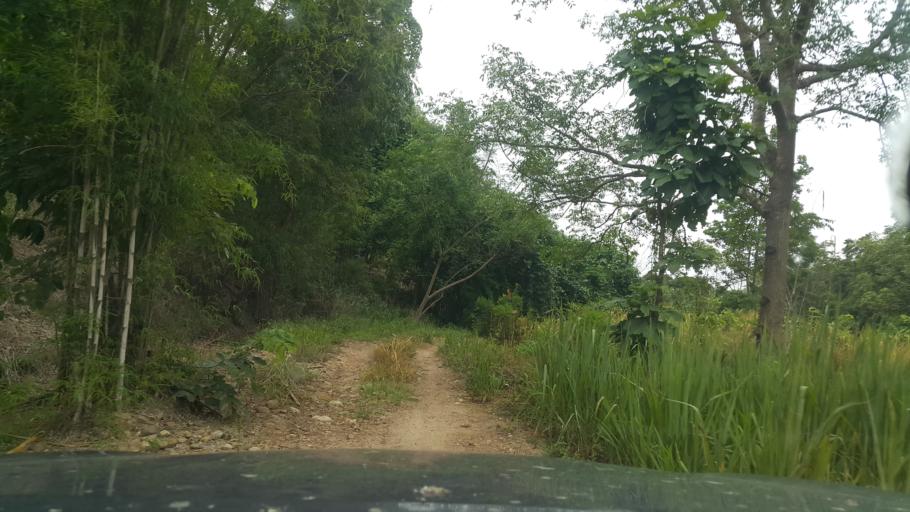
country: TH
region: Chiang Mai
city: Hang Dong
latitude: 18.6869
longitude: 98.8434
